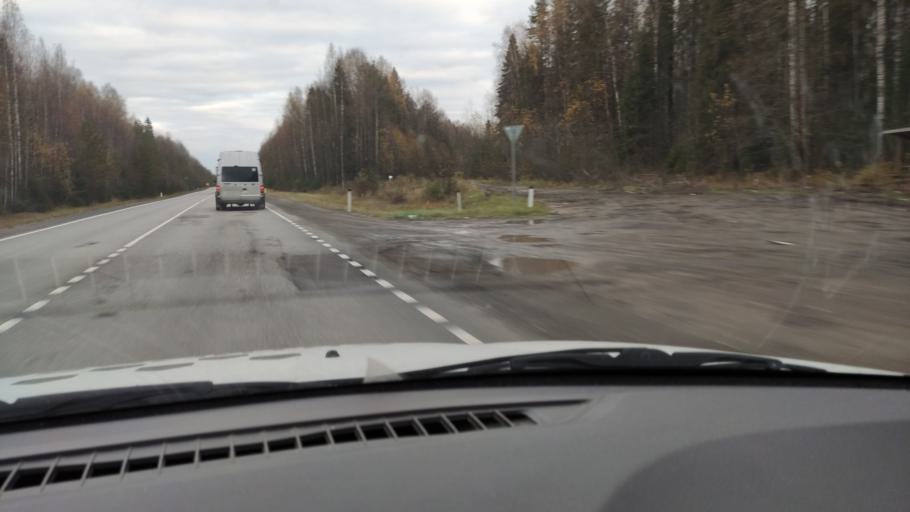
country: RU
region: Kirov
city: Chernaya Kholunitsa
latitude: 58.8587
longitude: 51.6397
